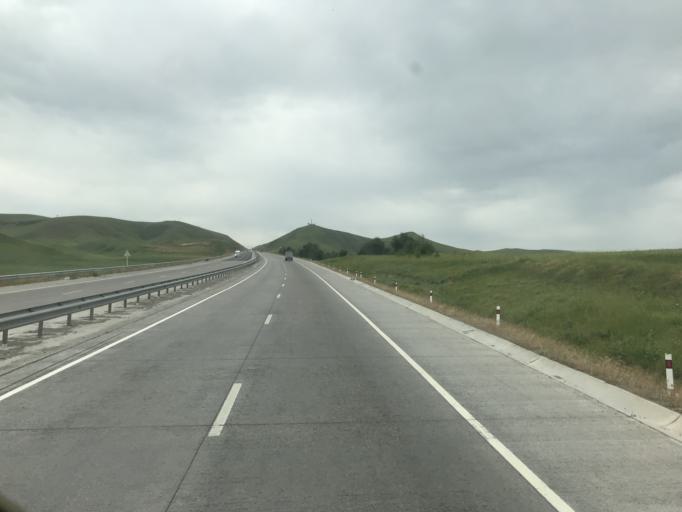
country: KZ
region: Ongtustik Qazaqstan
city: Qazyqurt
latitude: 42.0198
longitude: 69.4697
